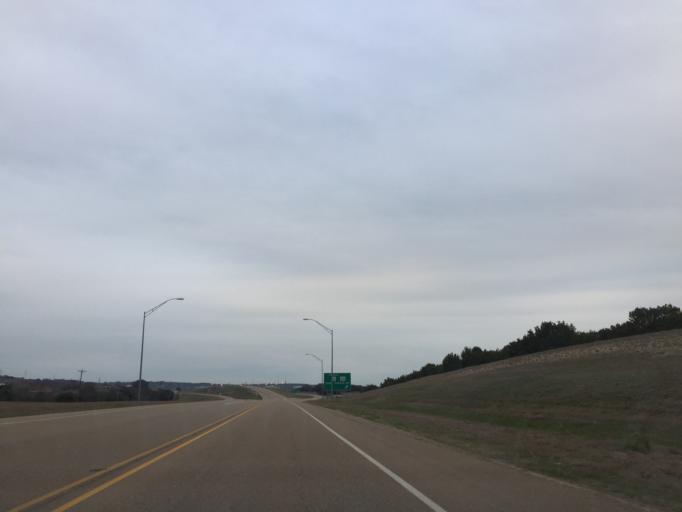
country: US
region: Texas
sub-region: Coryell County
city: Ames
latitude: 31.4881
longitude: -97.7390
